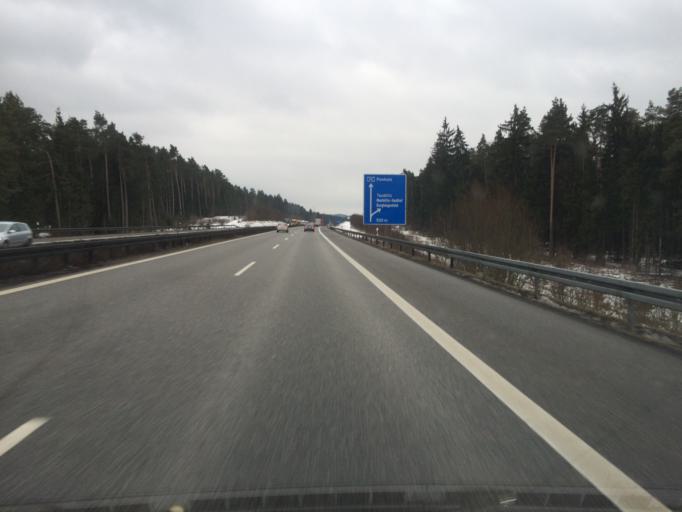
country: DE
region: Bavaria
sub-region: Upper Palatinate
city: Teublitz
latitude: 49.2278
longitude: 12.1308
